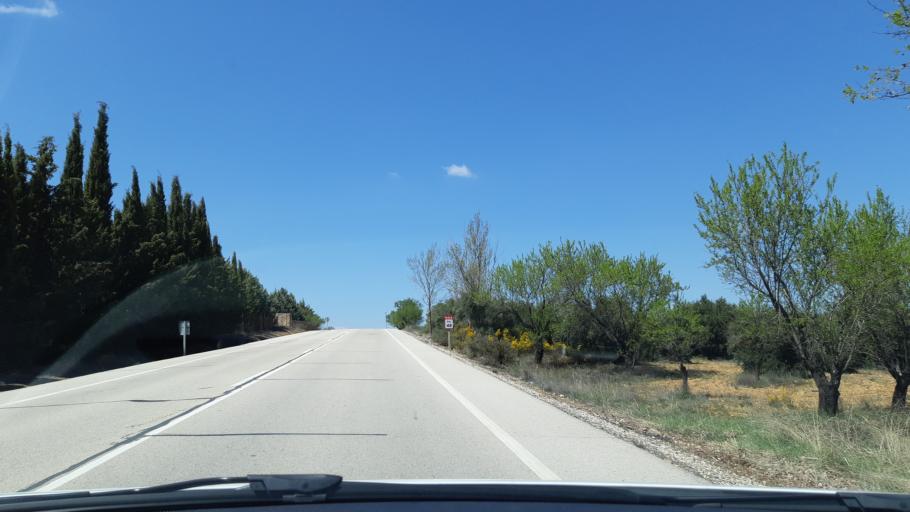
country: ES
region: Castille-La Mancha
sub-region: Provincia de Guadalajara
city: Cifuentes
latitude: 40.7882
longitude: -2.6342
